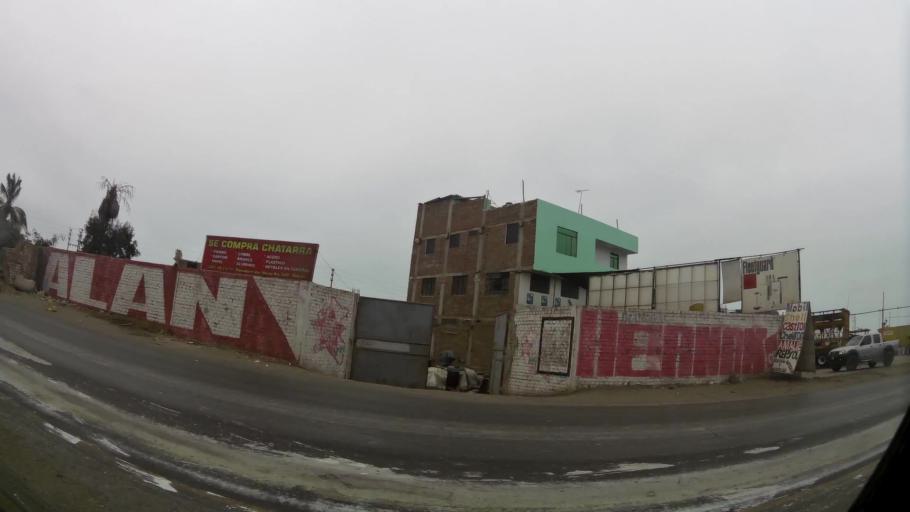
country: PE
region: La Libertad
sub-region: Provincia de Trujillo
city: Moche
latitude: -8.1655
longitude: -79.0089
